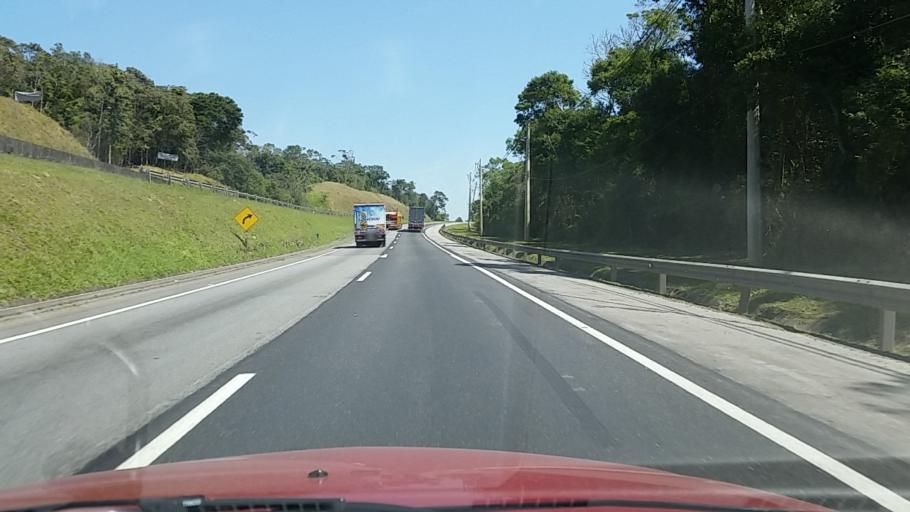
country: BR
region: Sao Paulo
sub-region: Juquitiba
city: Juquitiba
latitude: -23.9581
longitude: -47.1151
